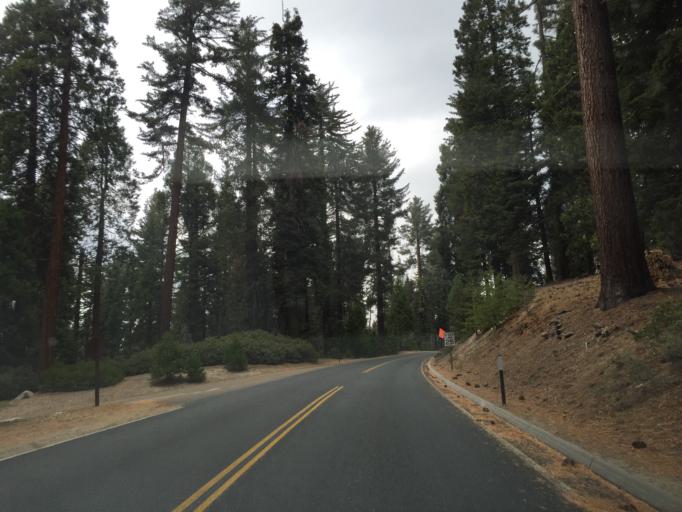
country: US
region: California
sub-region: Fresno County
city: Squaw Valley
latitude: 36.7372
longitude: -118.9643
